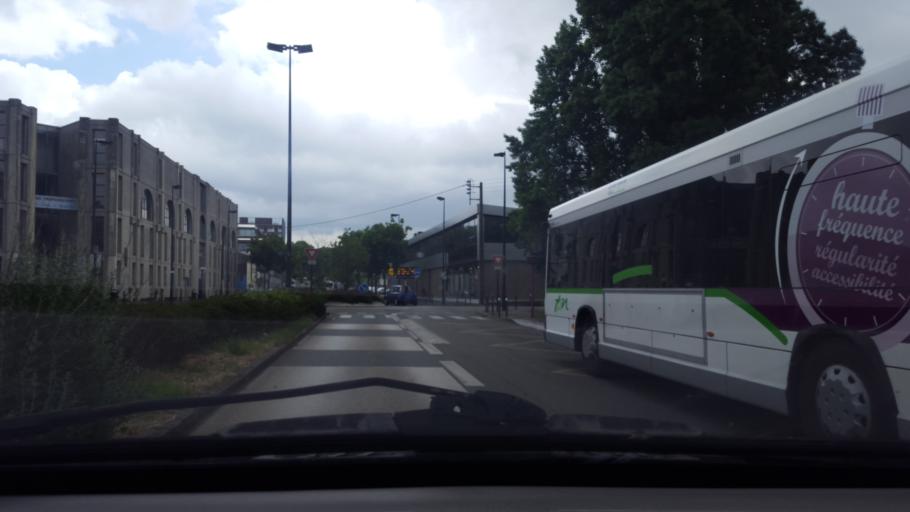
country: FR
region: Pays de la Loire
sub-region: Departement de la Loire-Atlantique
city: Bouguenais
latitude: 47.1978
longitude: -1.5933
